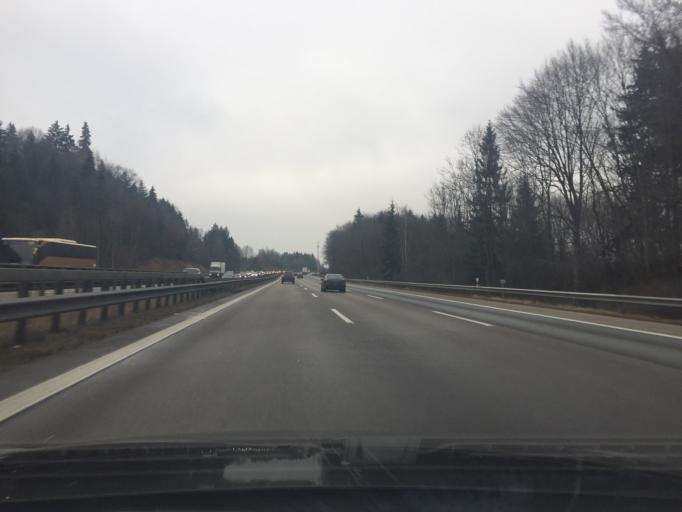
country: DE
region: Bavaria
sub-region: Upper Bavaria
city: Vagen
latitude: 47.8397
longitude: 11.8719
